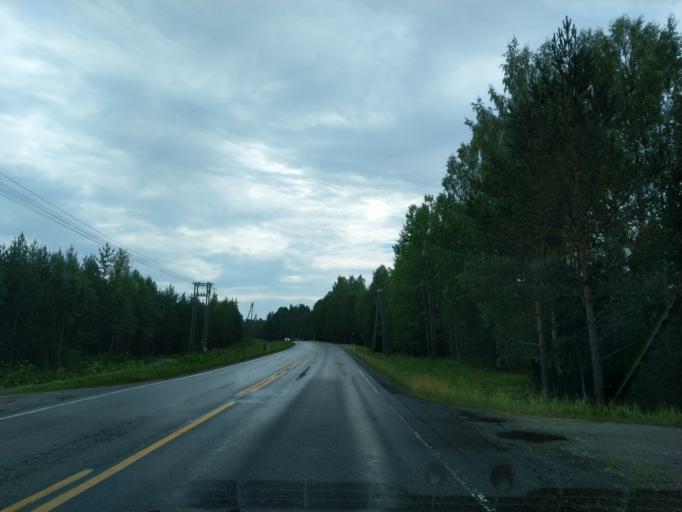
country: FI
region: Southern Savonia
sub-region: Savonlinna
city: Punkaharju
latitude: 61.6706
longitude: 29.4126
